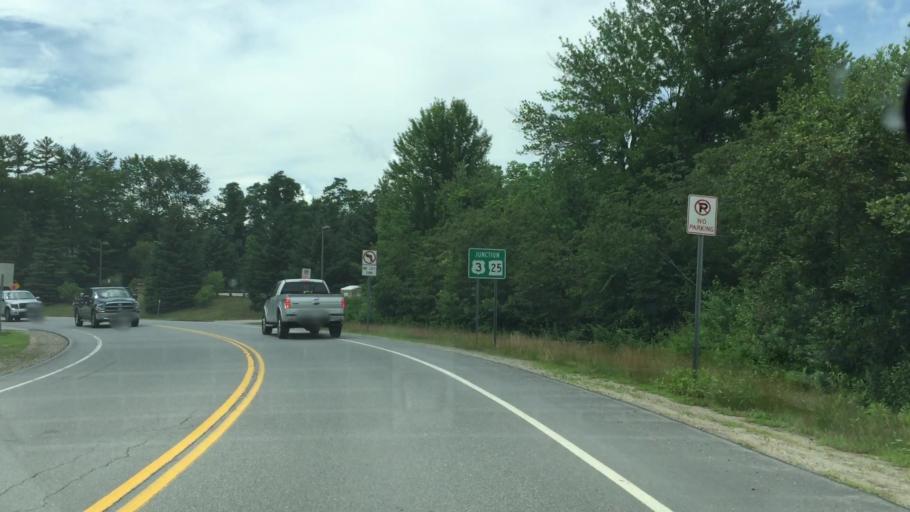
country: US
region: New Hampshire
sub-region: Grafton County
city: Holderness
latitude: 43.7331
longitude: -71.5879
